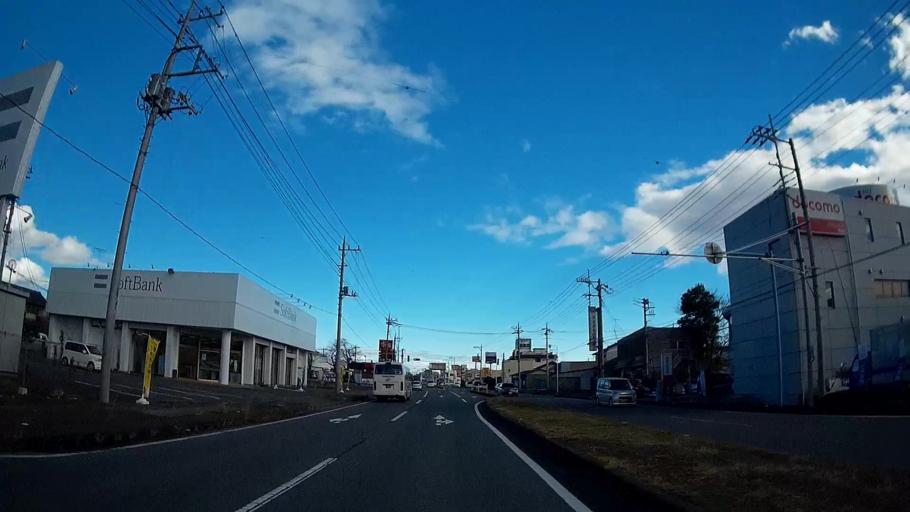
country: JP
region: Saitama
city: Yorii
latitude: 36.1212
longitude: 139.1909
